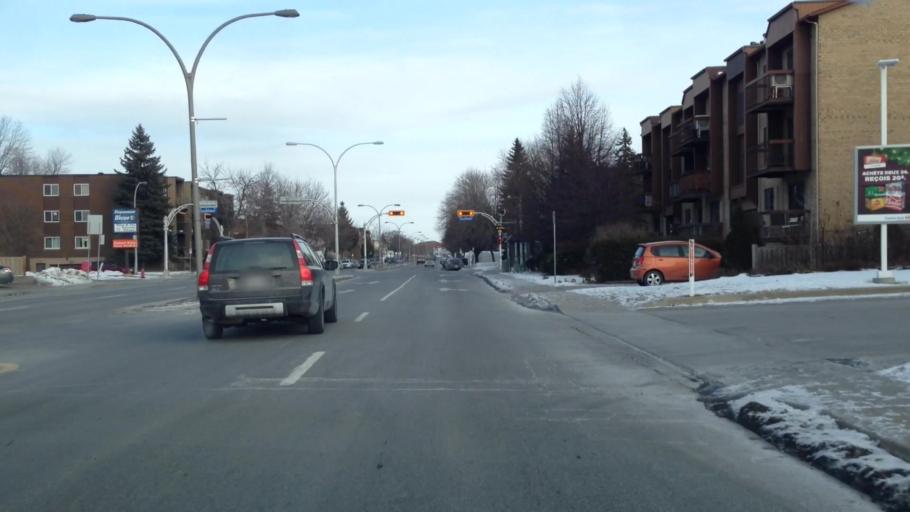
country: CA
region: Quebec
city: Dollard-Des Ormeaux
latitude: 45.5320
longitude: -73.7794
